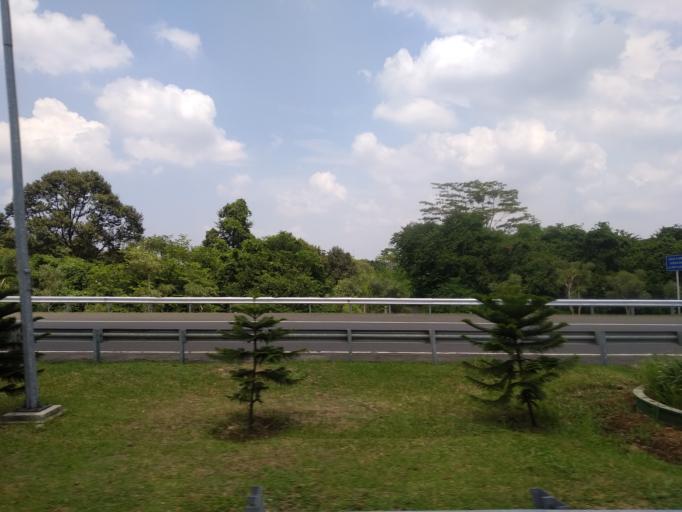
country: ID
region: West Java
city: Bogor
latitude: -6.5965
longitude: 106.8210
